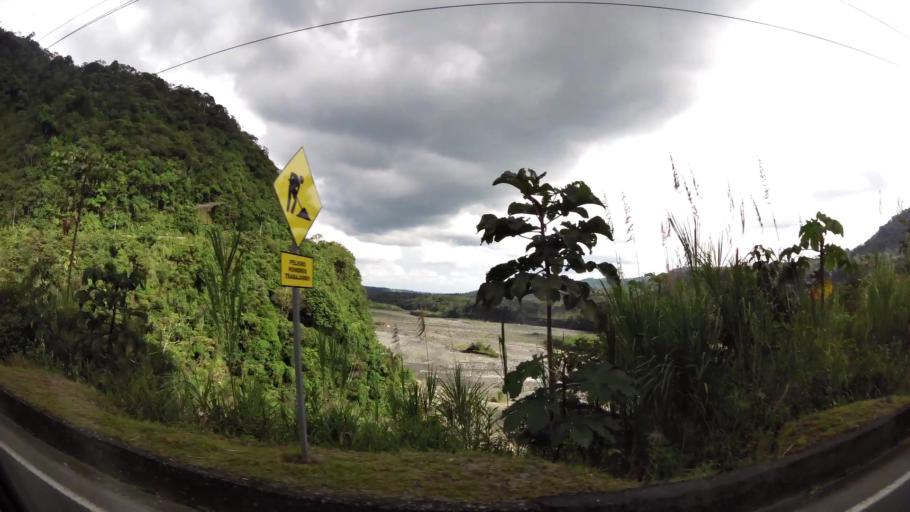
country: EC
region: Pastaza
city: Puyo
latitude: -1.4487
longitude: -78.1431
